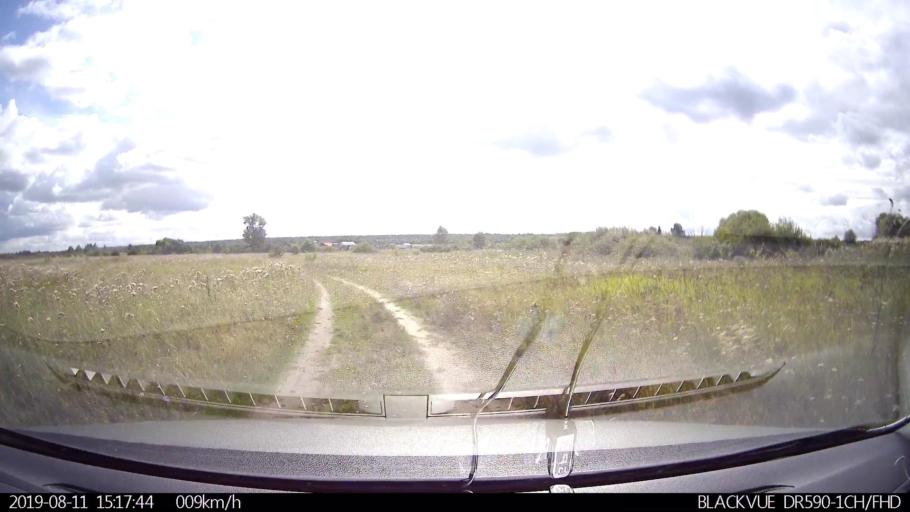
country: RU
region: Ulyanovsk
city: Ignatovka
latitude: 53.8443
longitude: 47.5867
